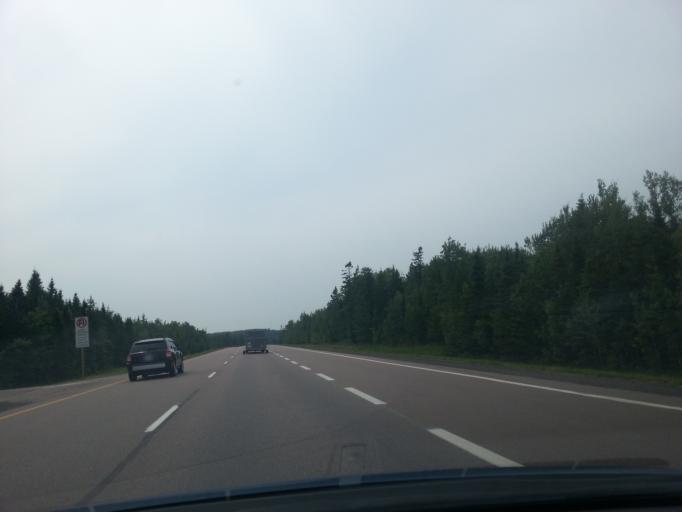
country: CA
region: New Brunswick
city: Salisbury
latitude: 46.0562
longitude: -65.0278
